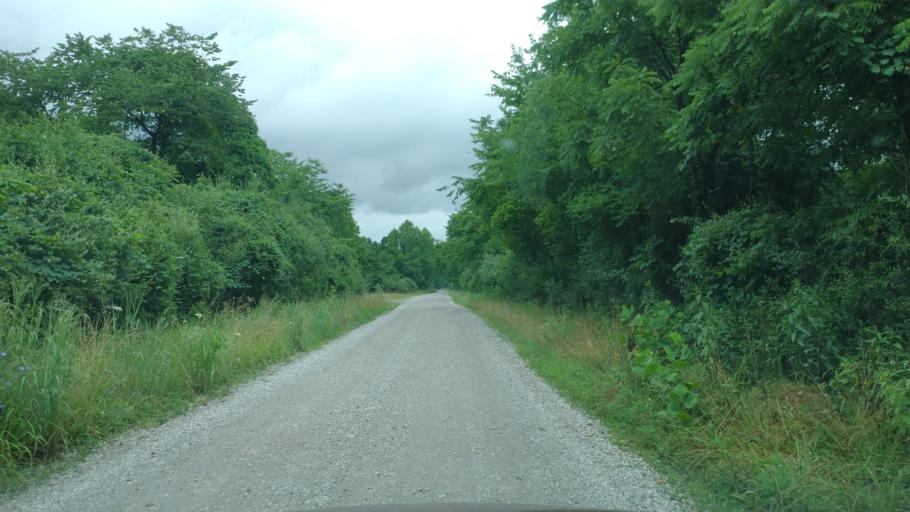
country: US
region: Ohio
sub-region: Meigs County
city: Middleport
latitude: 38.9254
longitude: -82.0696
